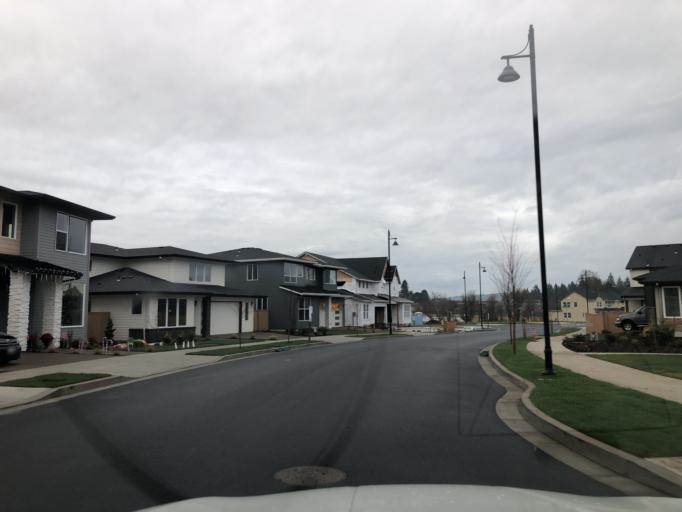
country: US
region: Oregon
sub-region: Washington County
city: Aloha
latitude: 45.4954
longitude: -122.9094
